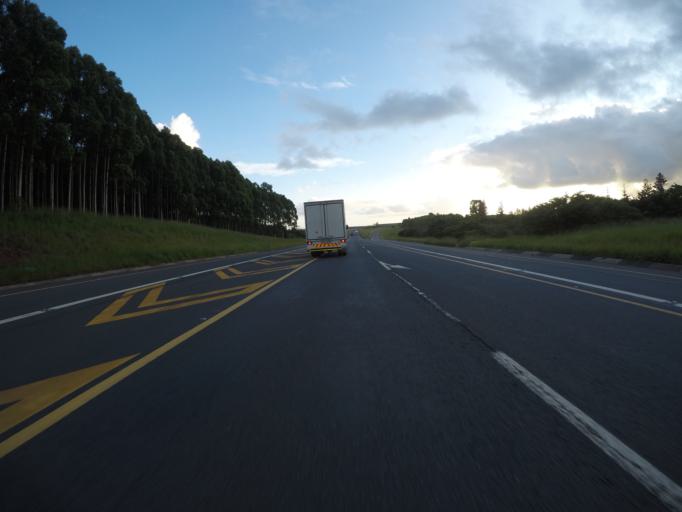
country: ZA
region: KwaZulu-Natal
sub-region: uThungulu District Municipality
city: KwaMbonambi
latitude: -28.5941
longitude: 32.0995
